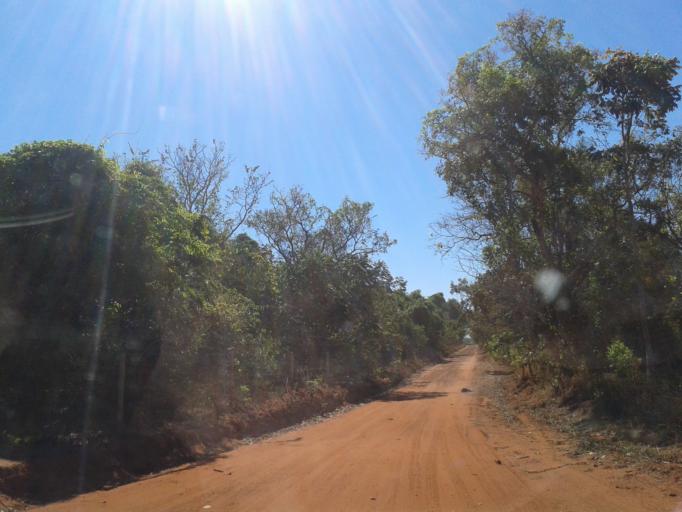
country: BR
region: Minas Gerais
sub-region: Ituiutaba
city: Ituiutaba
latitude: -19.0816
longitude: -49.3121
